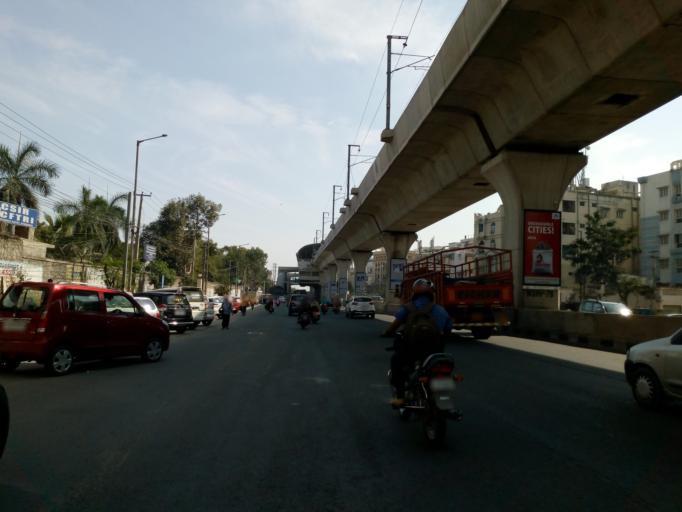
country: IN
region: Telangana
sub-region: Rangareddi
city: Uppal Kalan
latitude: 17.4166
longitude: 78.5445
